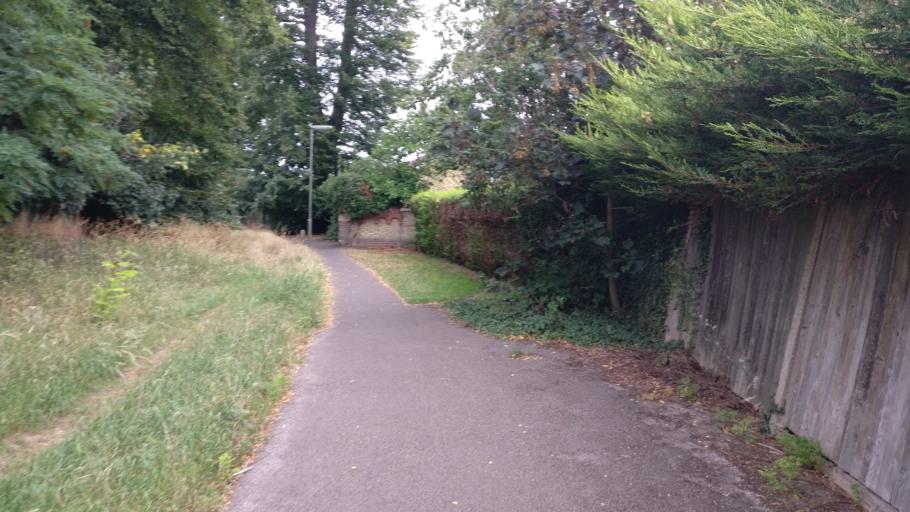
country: GB
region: England
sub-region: Surrey
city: Weybridge
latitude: 51.3736
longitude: -0.4465
